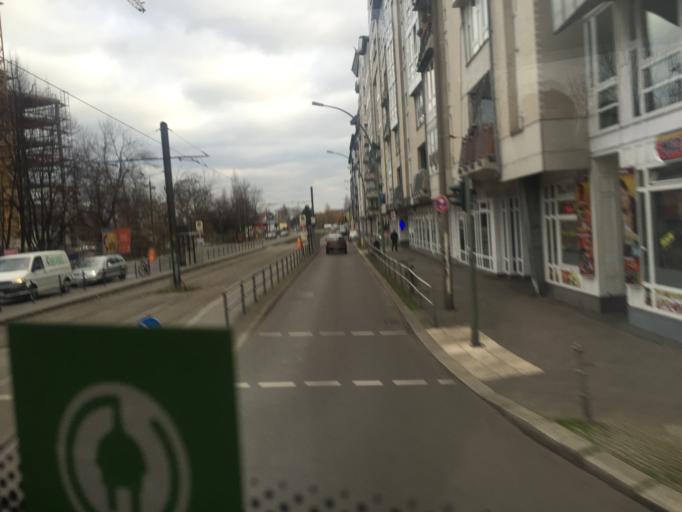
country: DE
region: Berlin
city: Heinersdorf
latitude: 52.5564
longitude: 13.4294
